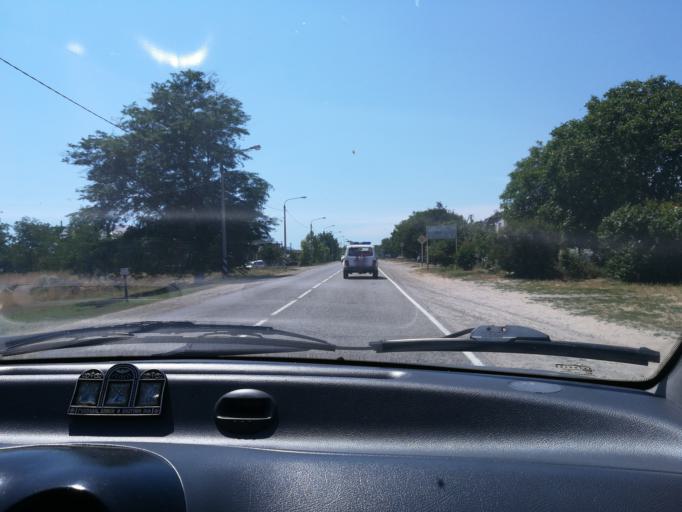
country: RU
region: Krasnodarskiy
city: Blagovetschenskaya
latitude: 45.0555
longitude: 37.1479
